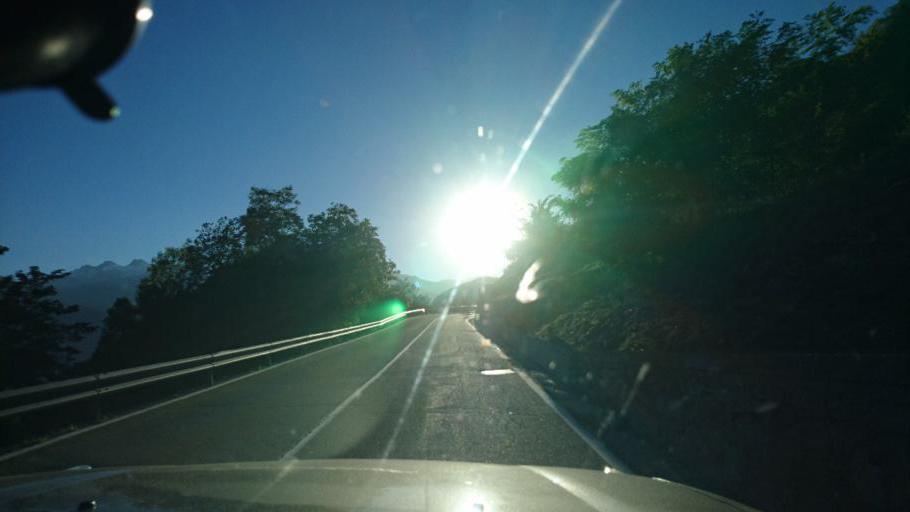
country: IT
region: Aosta Valley
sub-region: Valle d'Aosta
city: Villeneuve
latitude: 45.7109
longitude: 7.1919
